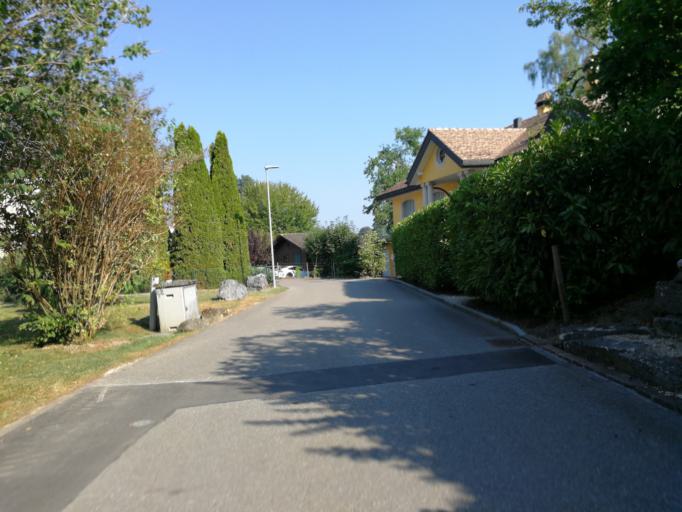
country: CH
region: Saint Gallen
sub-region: Wahlkreis See-Gaster
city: Rapperswil
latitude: 47.2039
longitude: 8.8003
